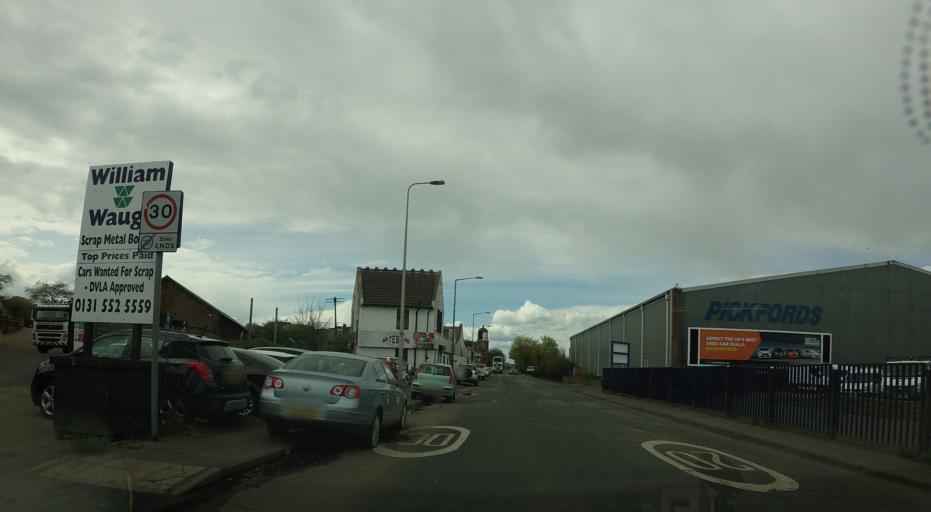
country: GB
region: Scotland
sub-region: Edinburgh
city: Edinburgh
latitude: 55.9814
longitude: -3.2260
